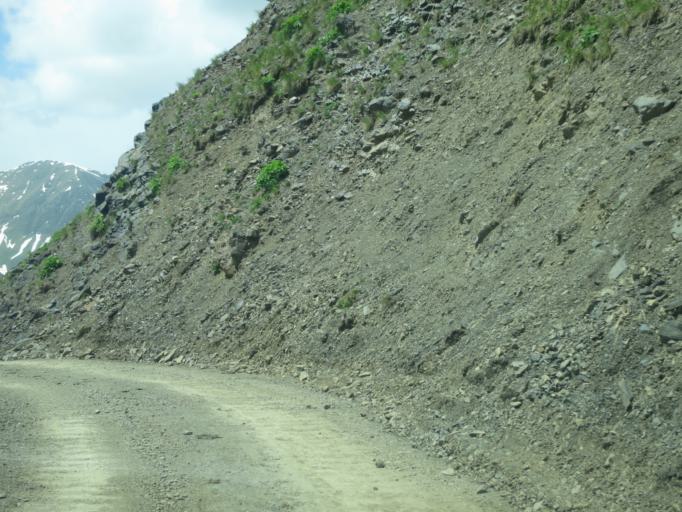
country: GE
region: Kakheti
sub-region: Telavi
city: Telavi
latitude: 42.2709
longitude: 45.4945
